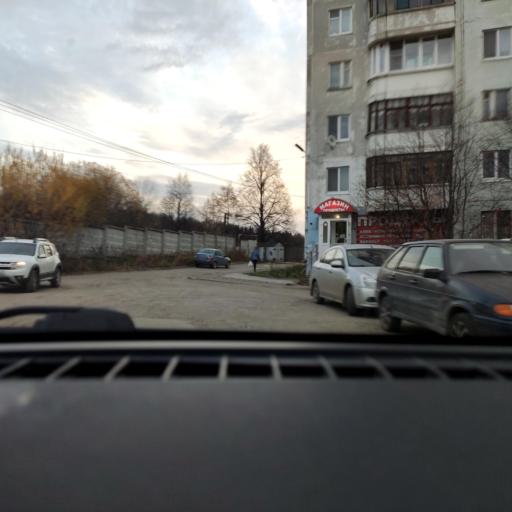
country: RU
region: Perm
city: Froly
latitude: 57.9452
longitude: 56.2730
